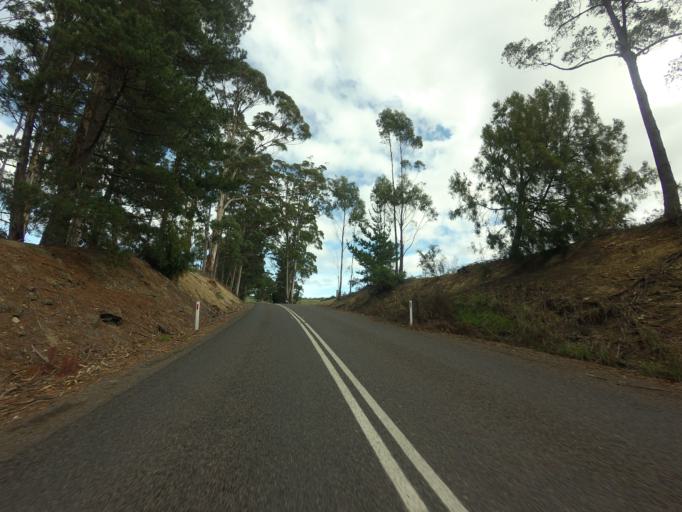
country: AU
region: Tasmania
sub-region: Clarence
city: Sandford
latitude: -43.0626
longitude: 147.7519
